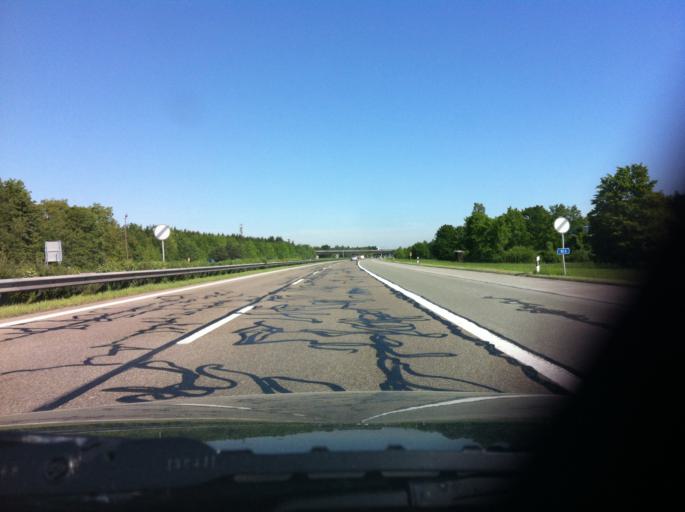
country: DE
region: Bavaria
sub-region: Upper Bavaria
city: Brunnthal
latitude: 48.0173
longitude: 11.6630
